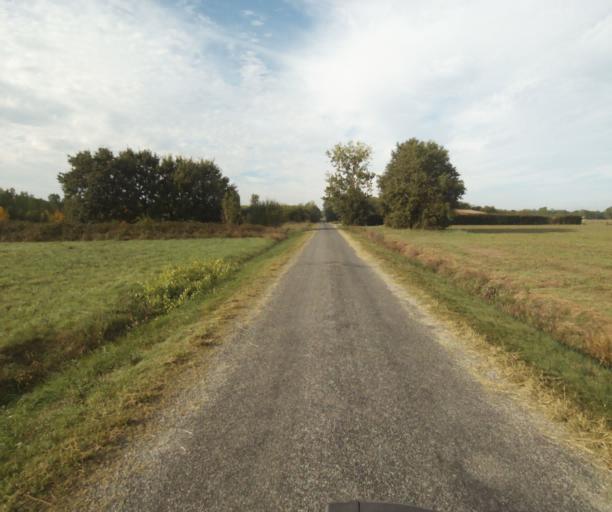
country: FR
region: Midi-Pyrenees
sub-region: Departement du Tarn-et-Garonne
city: Montech
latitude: 43.9743
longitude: 1.2415
